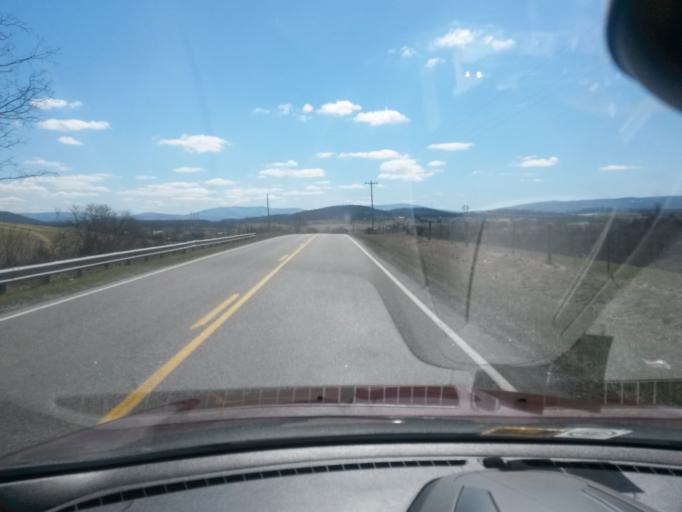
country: US
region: Virginia
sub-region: Augusta County
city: Jolivue
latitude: 38.0687
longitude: -79.0769
